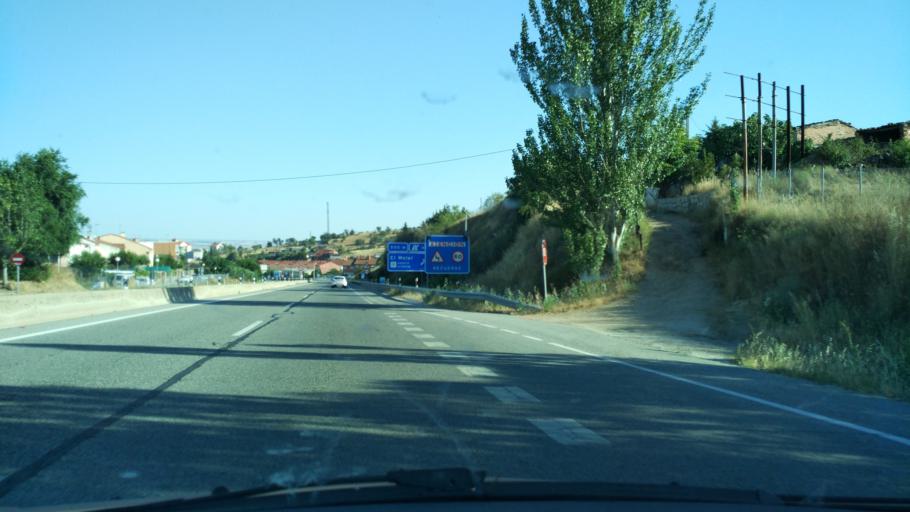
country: ES
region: Madrid
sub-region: Provincia de Madrid
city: El Molar
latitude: 40.7363
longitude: -3.5866
